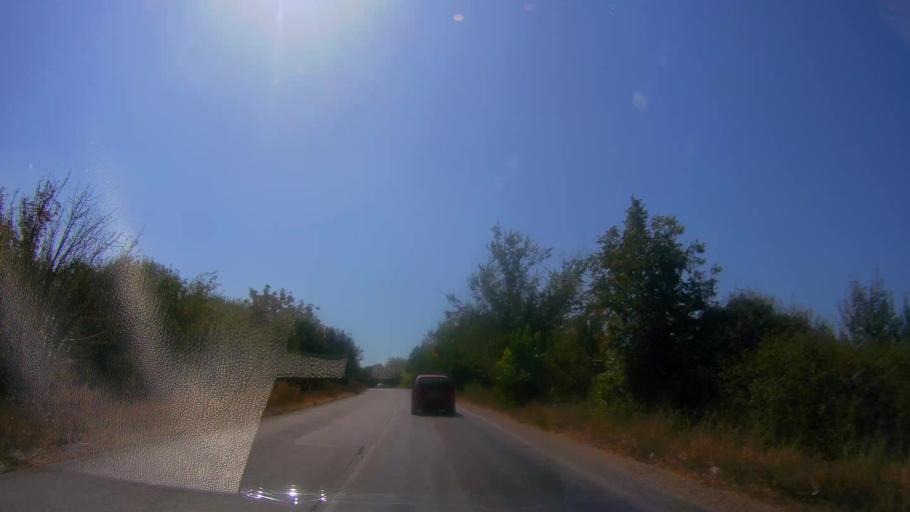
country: BG
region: Veliko Turnovo
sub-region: Obshtina Gorna Oryakhovitsa
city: Purvomaytsi
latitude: 43.2579
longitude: 25.6423
